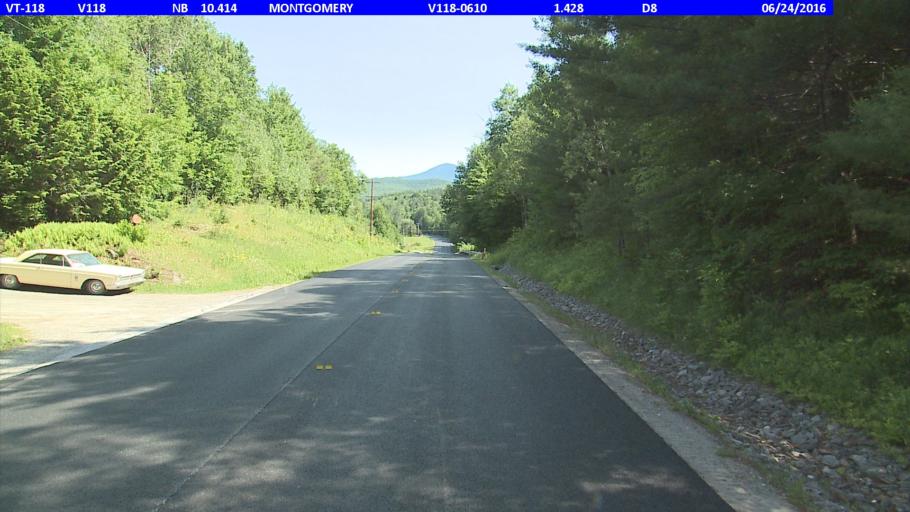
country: US
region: Vermont
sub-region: Franklin County
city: Richford
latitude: 44.8191
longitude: -72.6131
